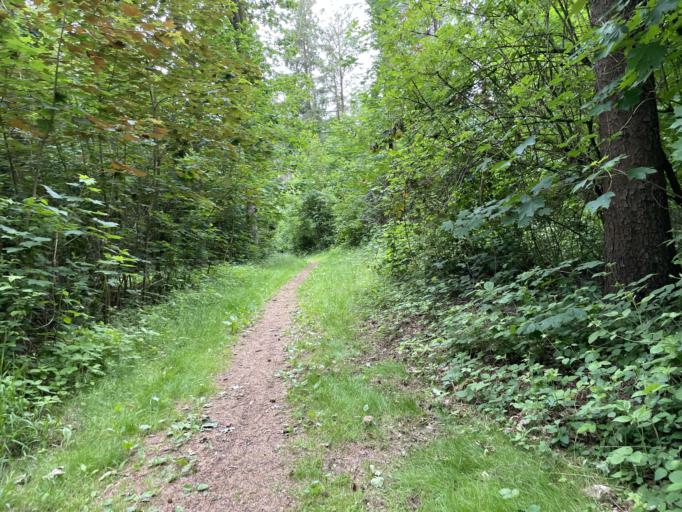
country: DE
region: Schleswig-Holstein
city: Mildstedt
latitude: 54.4722
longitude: 9.0758
